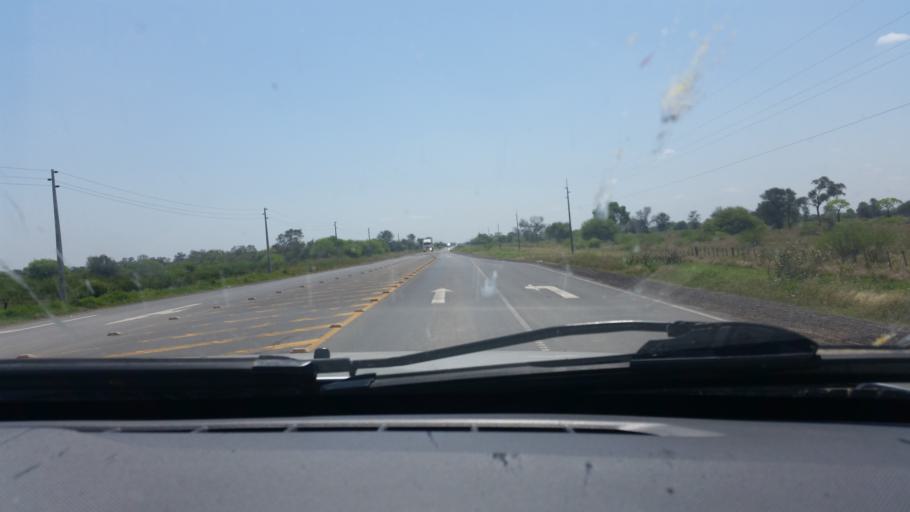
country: PY
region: Boqueron
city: Filadelfia
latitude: -22.4651
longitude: -60.0119
